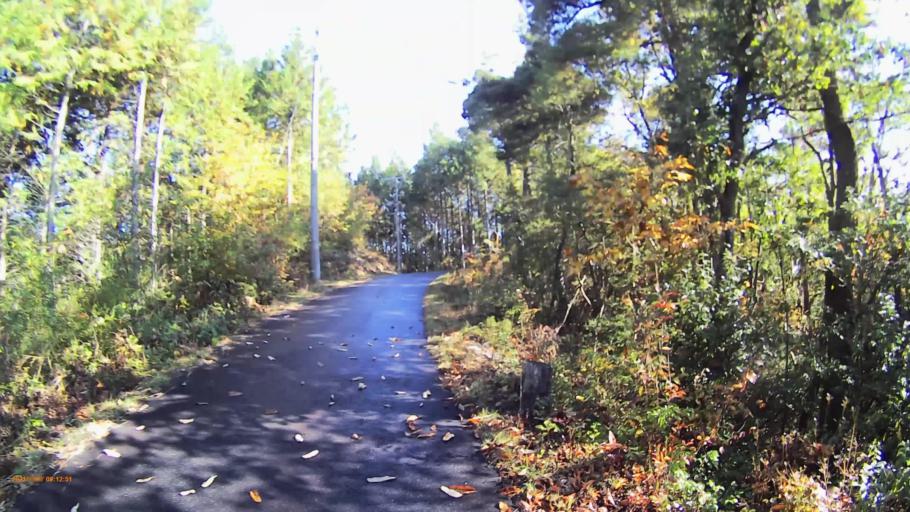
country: JP
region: Gifu
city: Mizunami
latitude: 35.4428
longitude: 137.3546
